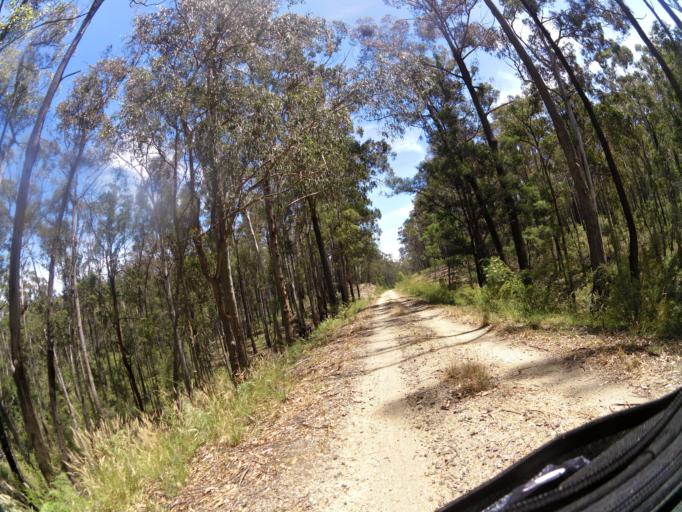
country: AU
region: Victoria
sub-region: East Gippsland
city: Lakes Entrance
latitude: -37.7599
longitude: 147.9365
